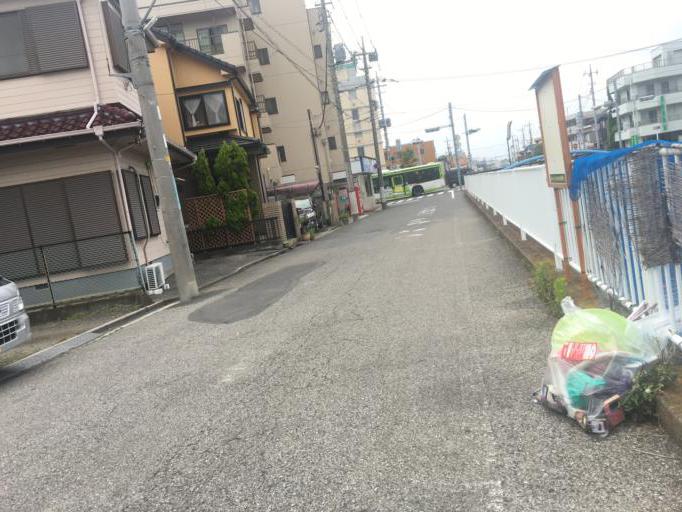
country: JP
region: Saitama
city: Kawaguchi
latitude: 35.8255
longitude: 139.7179
